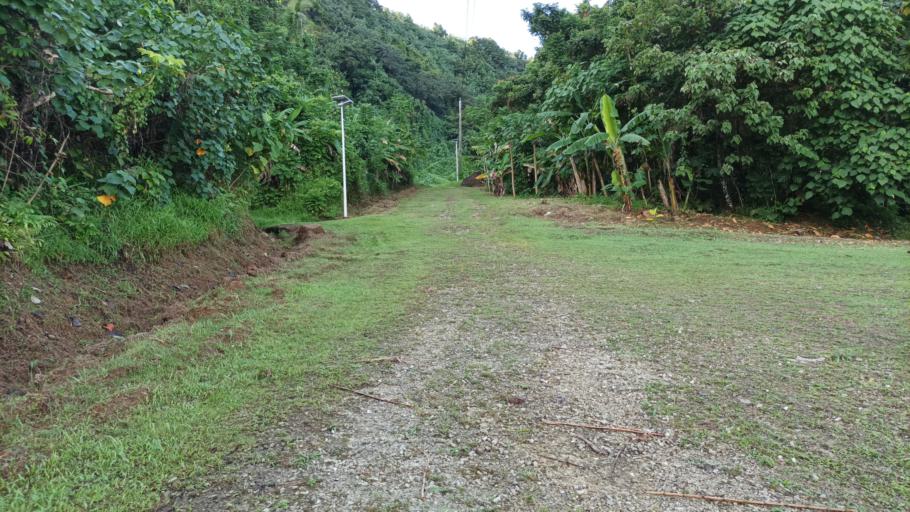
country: FM
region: Pohnpei
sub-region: Kolonia Municipality
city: Kolonia Town
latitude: 6.9657
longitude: 158.1932
